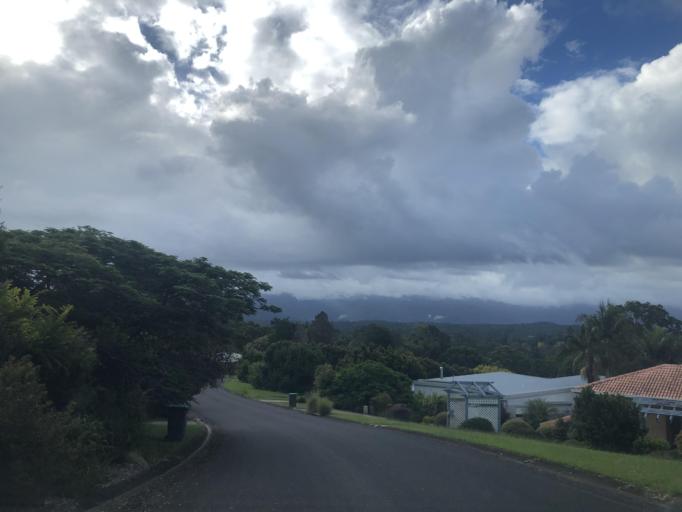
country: AU
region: New South Wales
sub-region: Bellingen
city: Bellingen
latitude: -30.4606
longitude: 152.9022
